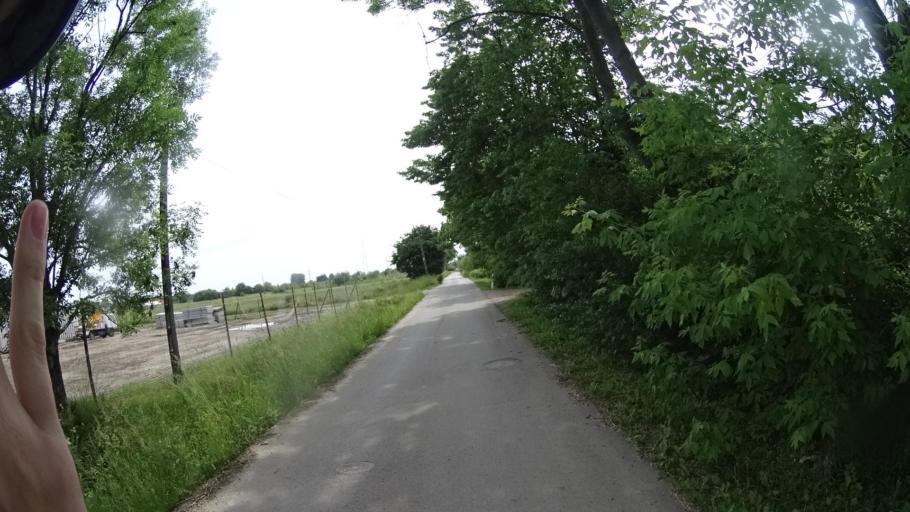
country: PL
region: Masovian Voivodeship
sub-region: Powiat pruszkowski
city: Michalowice
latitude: 52.1795
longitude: 20.8919
